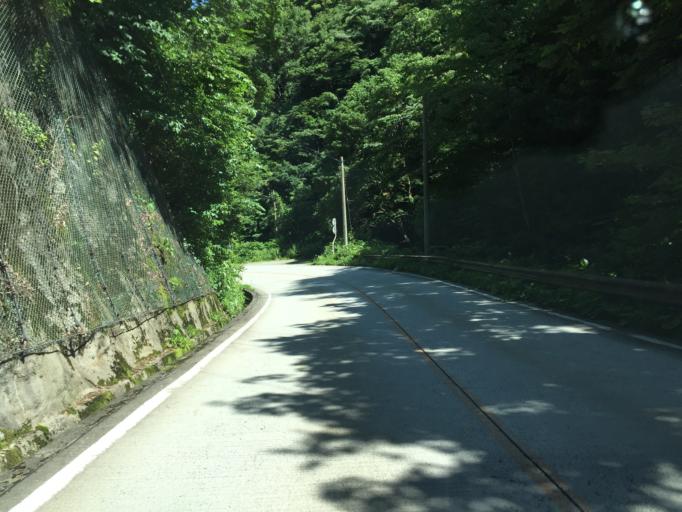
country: JP
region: Fukushima
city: Fukushima-shi
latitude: 37.7491
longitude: 140.3298
